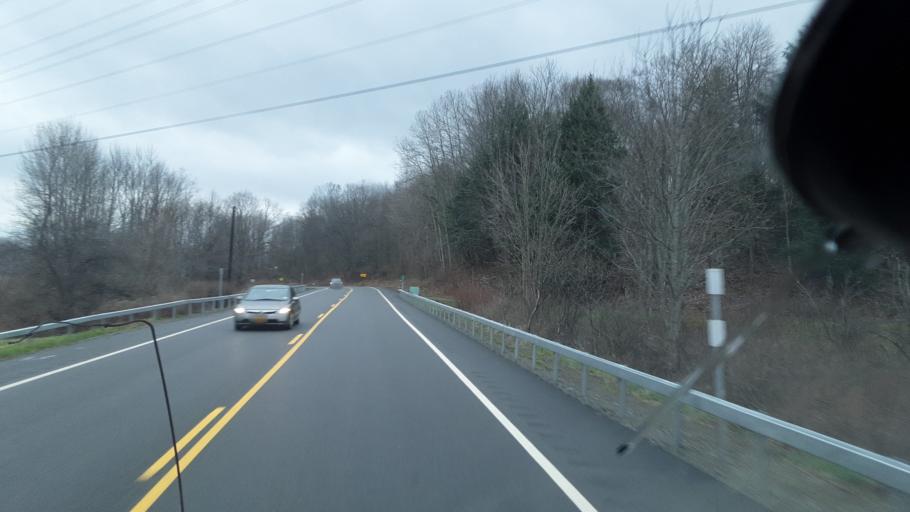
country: US
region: New York
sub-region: Allegany County
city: Houghton
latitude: 42.3577
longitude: -78.1280
